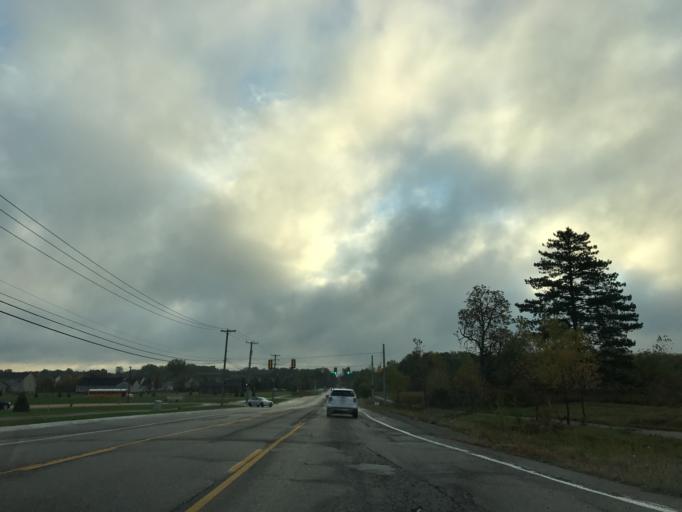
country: US
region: Michigan
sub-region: Oakland County
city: South Lyon
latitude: 42.4762
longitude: -83.6221
